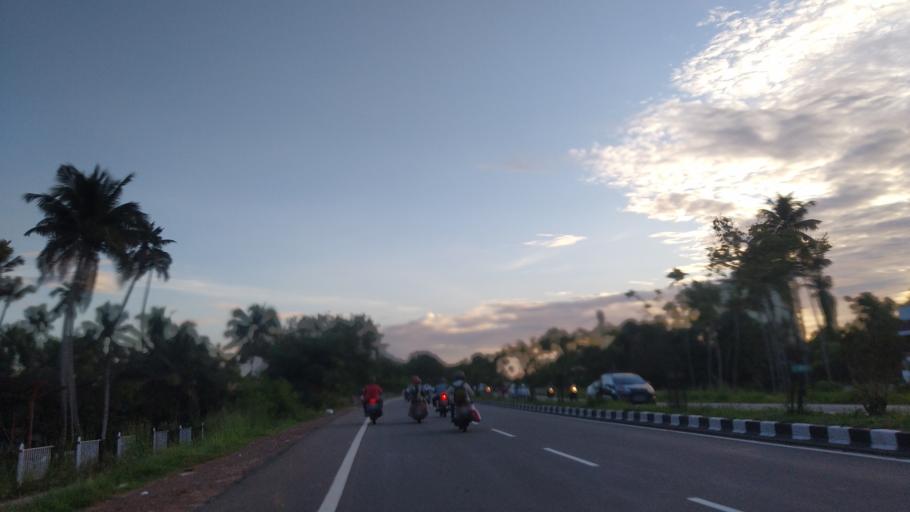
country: IN
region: Kerala
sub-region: Ernakulam
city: Elur
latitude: 10.0568
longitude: 76.2844
